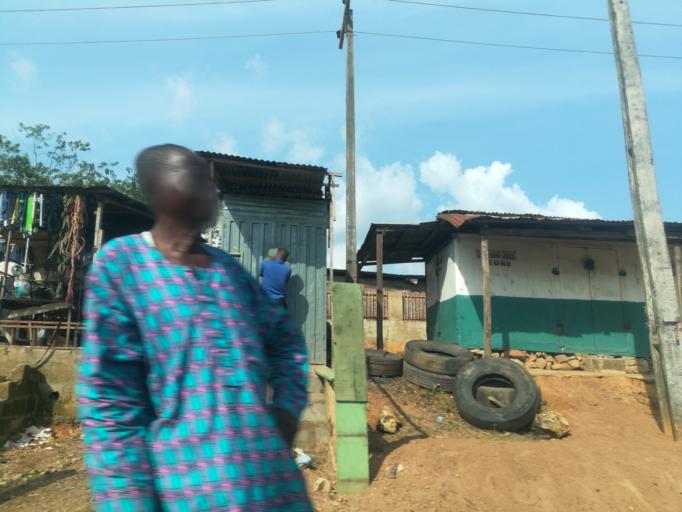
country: NG
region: Oyo
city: Ido
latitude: 7.3953
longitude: 3.8106
